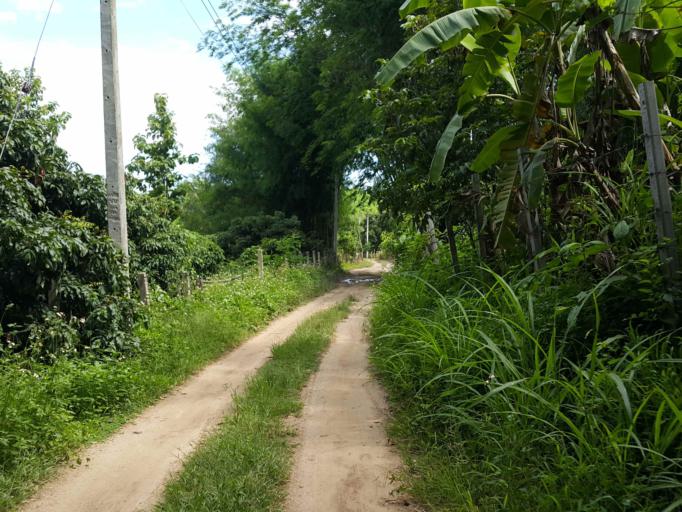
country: TH
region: Chiang Mai
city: Mae Taeng
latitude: 18.9556
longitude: 98.9164
